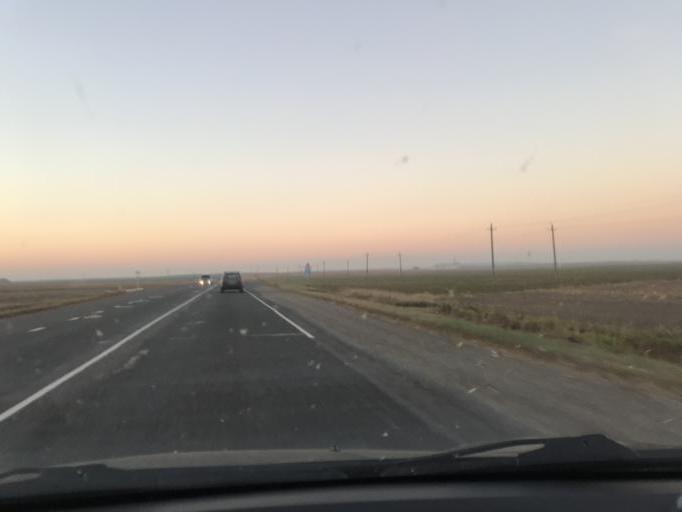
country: BY
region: Gomel
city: Horad Rechytsa
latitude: 52.2749
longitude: 30.4756
